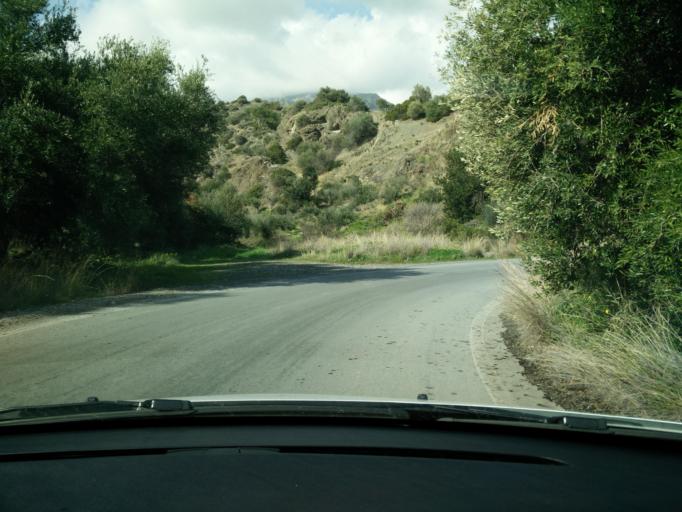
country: GR
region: Crete
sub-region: Nomos Lasithiou
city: Gra Liyia
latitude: 35.0224
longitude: 25.5818
